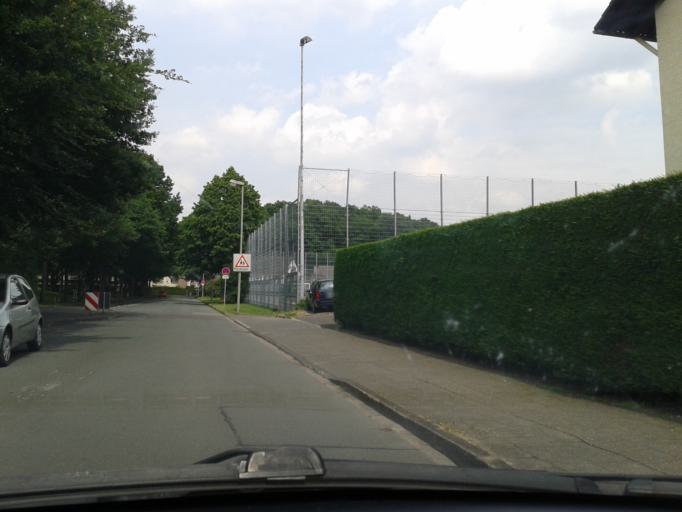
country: DE
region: North Rhine-Westphalia
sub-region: Regierungsbezirk Detmold
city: Paderborn
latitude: 51.7379
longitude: 8.6816
